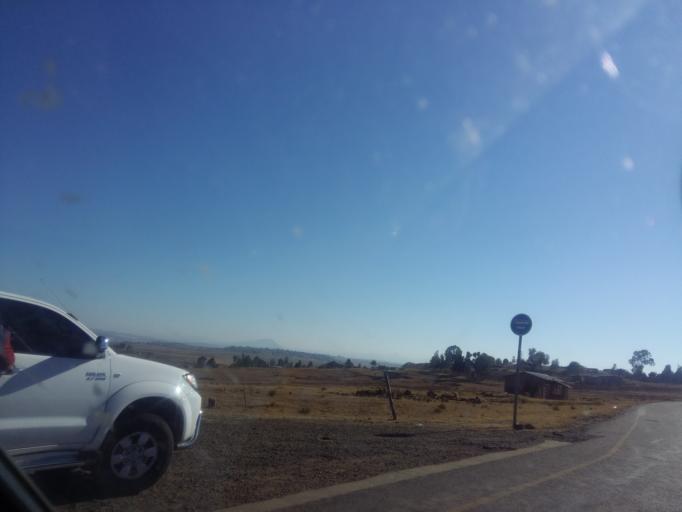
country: LS
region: Mafeteng
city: Mafeteng
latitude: -29.6892
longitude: 27.2799
